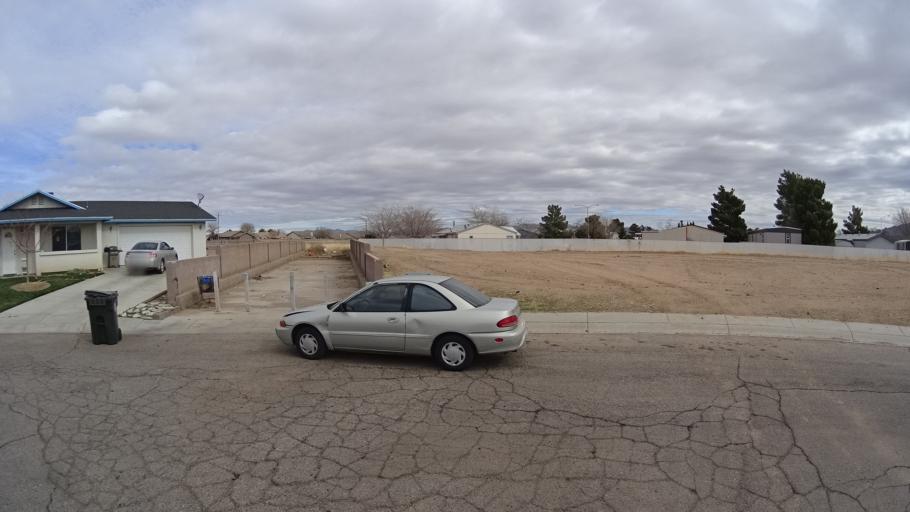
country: US
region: Arizona
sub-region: Mohave County
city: New Kingman-Butler
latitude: 35.2308
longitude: -114.0319
